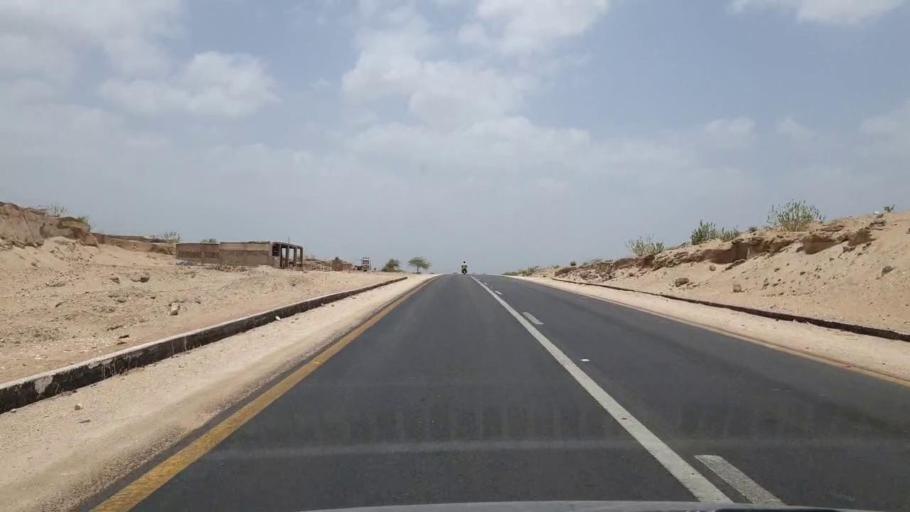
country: PK
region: Sindh
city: Naukot
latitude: 24.8398
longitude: 69.4591
